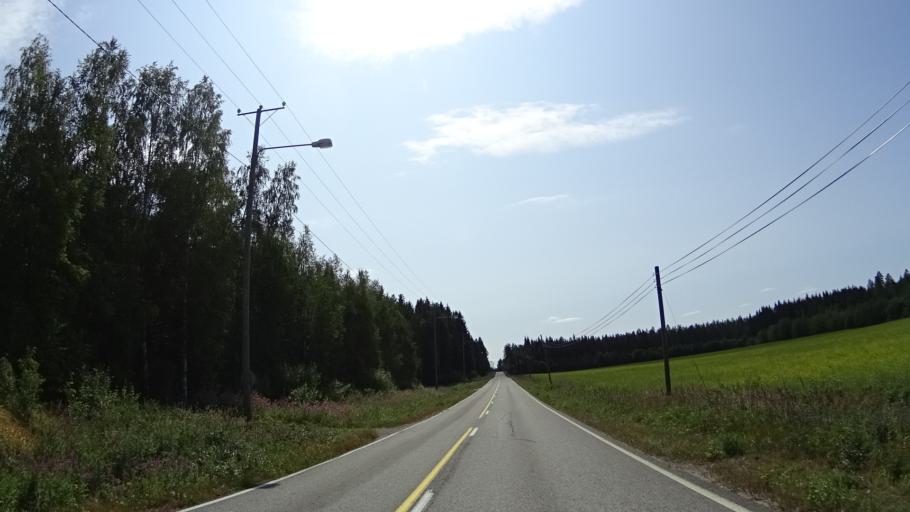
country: FI
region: Pirkanmaa
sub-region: Ylae-Pirkanmaa
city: Maenttae
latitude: 61.8891
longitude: 24.7920
